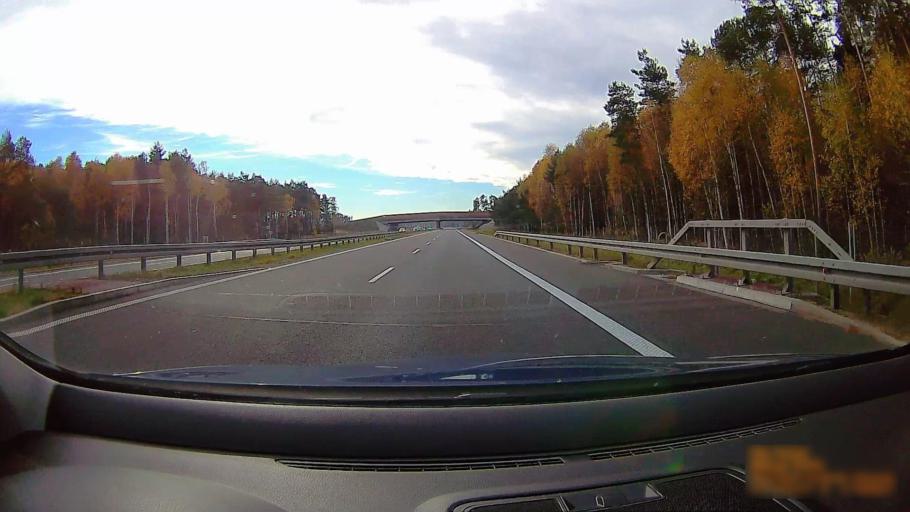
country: PL
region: Greater Poland Voivodeship
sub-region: Powiat ostrowski
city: Przygodzice
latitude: 51.5643
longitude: 17.8468
